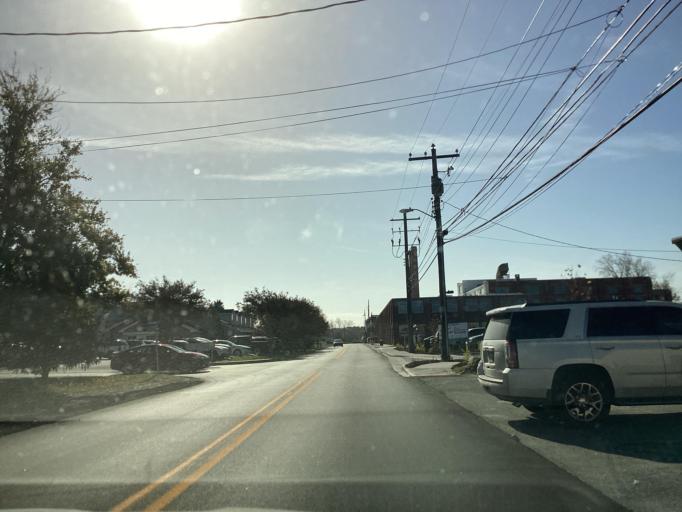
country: US
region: Maryland
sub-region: Dorchester County
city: Cambridge
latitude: 38.5634
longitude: -76.0677
